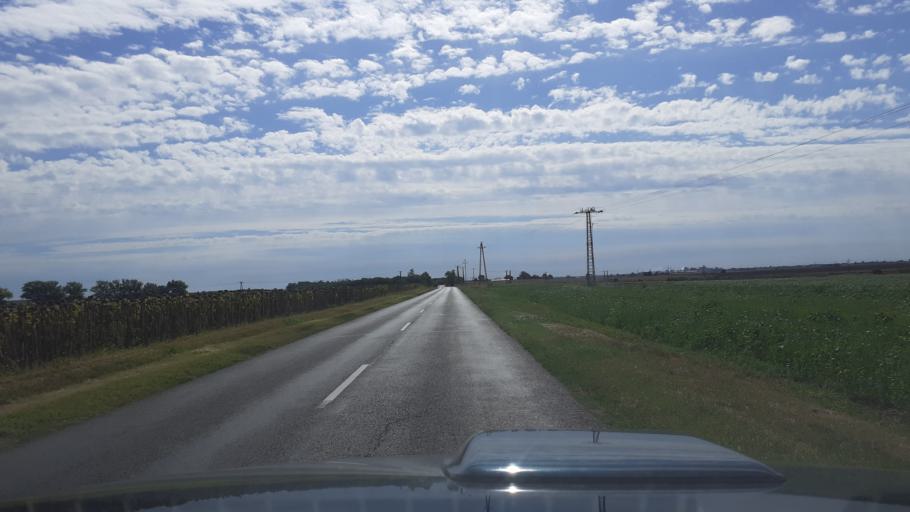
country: HU
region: Fejer
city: Pusztaszabolcs
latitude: 47.1274
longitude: 18.6807
